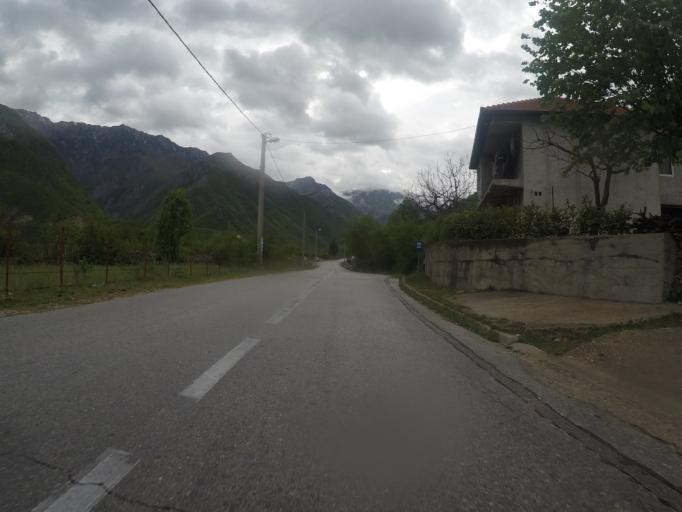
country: BA
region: Federation of Bosnia and Herzegovina
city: Siroki Brijeg
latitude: 43.5401
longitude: 17.6295
